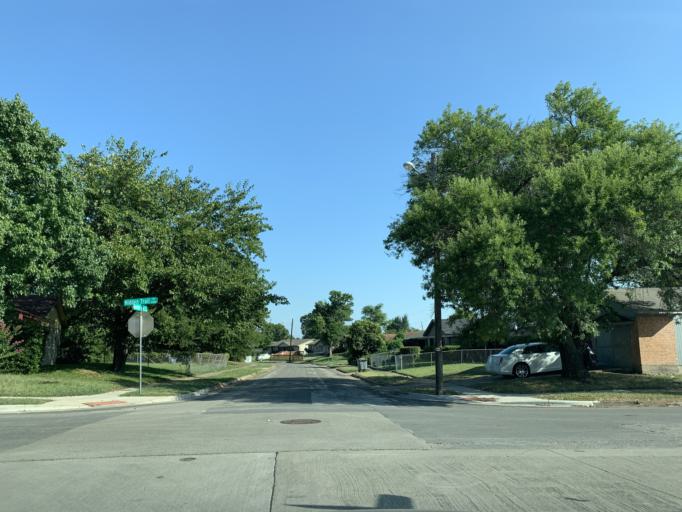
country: US
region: Texas
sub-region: Dallas County
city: Hutchins
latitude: 32.6622
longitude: -96.7683
